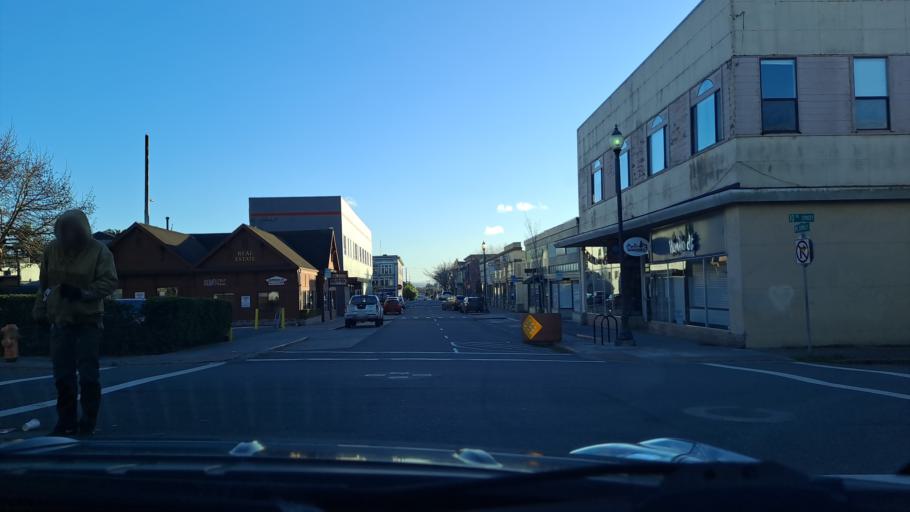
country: US
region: California
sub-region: Humboldt County
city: Arcata
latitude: 40.8699
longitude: -124.0865
